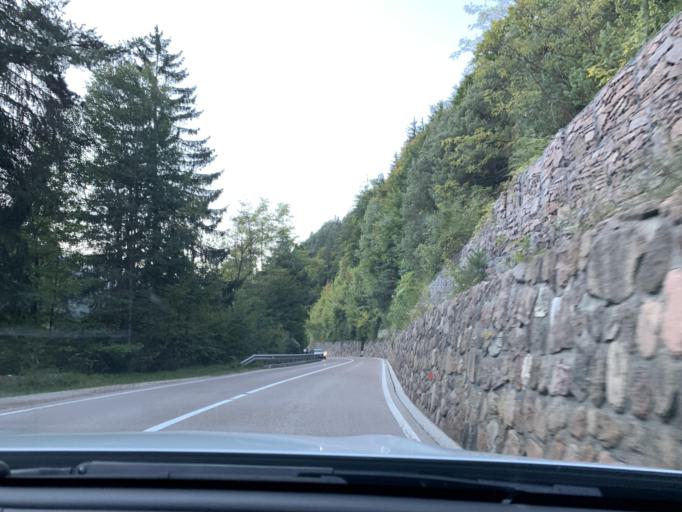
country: IT
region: Trentino-Alto Adige
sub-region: Bolzano
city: Nova Ponente
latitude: 46.4437
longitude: 11.4616
